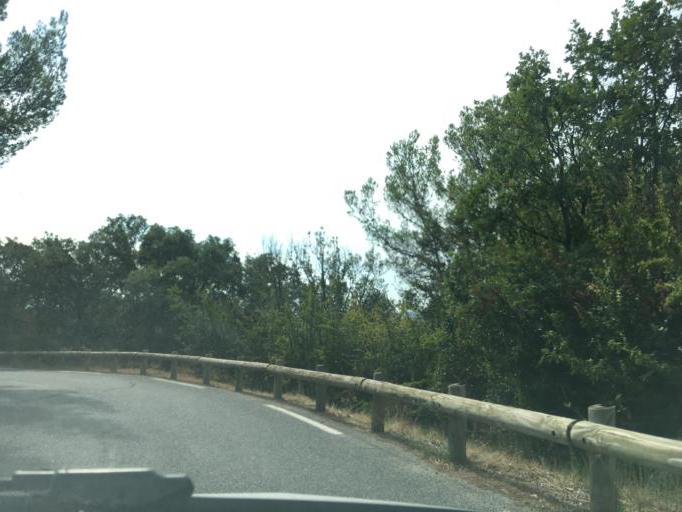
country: FR
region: Provence-Alpes-Cote d'Azur
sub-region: Departement du Var
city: Taradeau
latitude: 43.4570
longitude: 6.4256
